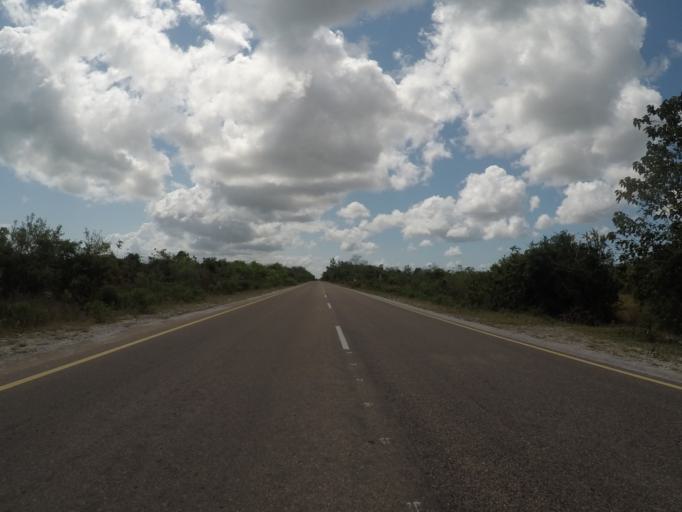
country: TZ
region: Zanzibar Central/South
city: Koani
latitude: -6.2641
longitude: 39.3603
